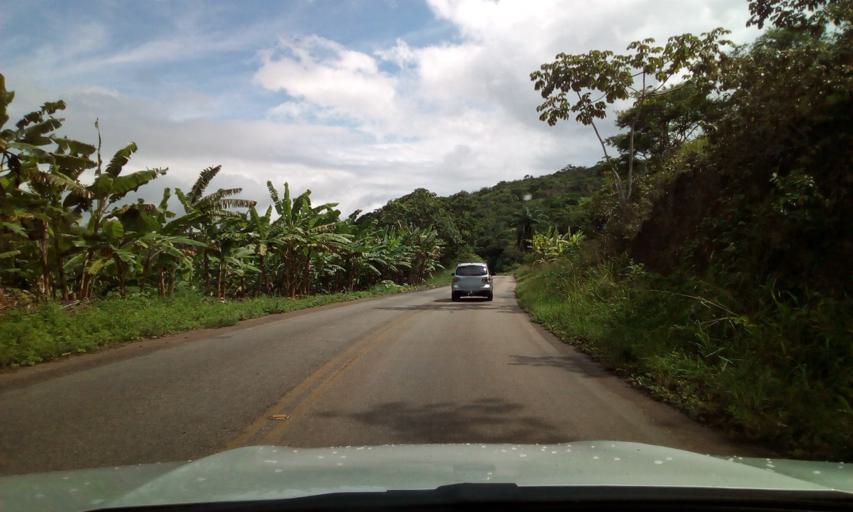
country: BR
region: Paraiba
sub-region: Areia
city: Areia
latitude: -6.9290
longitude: -35.6468
